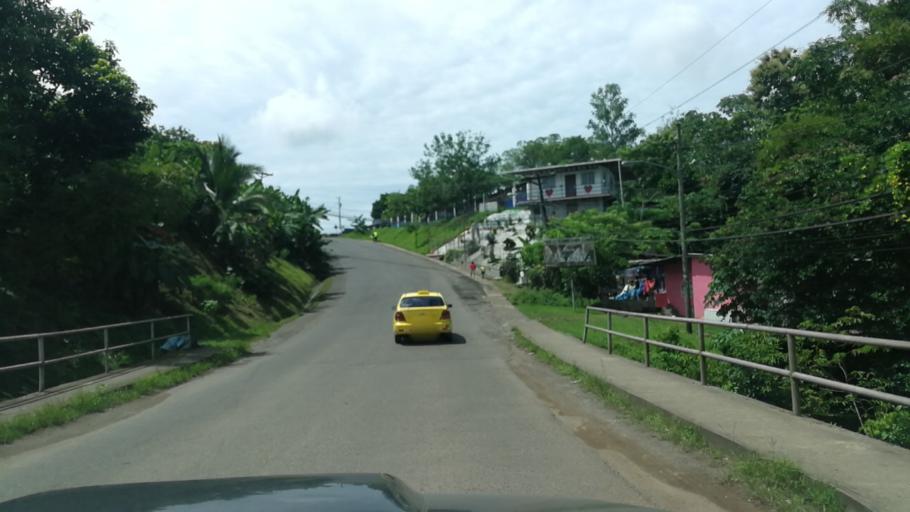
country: PA
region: Panama
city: Tocumen
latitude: 9.0955
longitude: -79.4084
